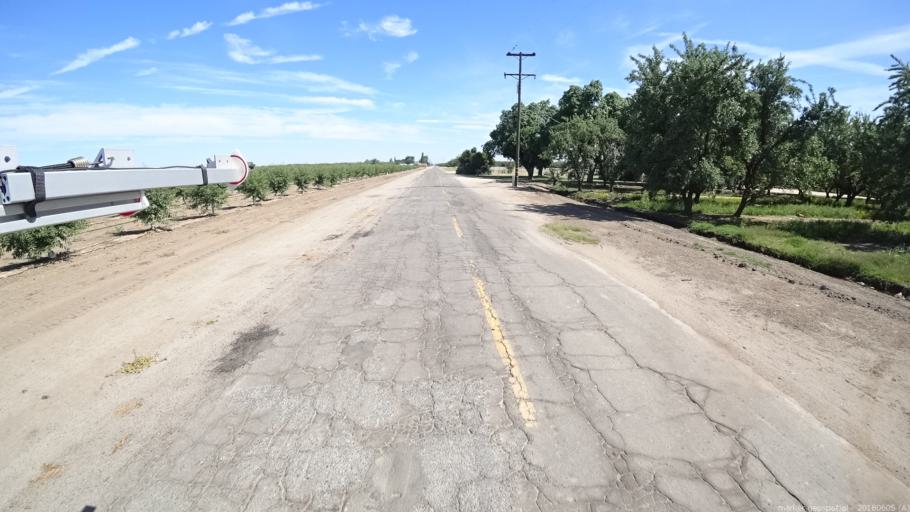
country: US
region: California
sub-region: Madera County
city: Chowchilla
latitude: 37.0337
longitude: -120.4013
